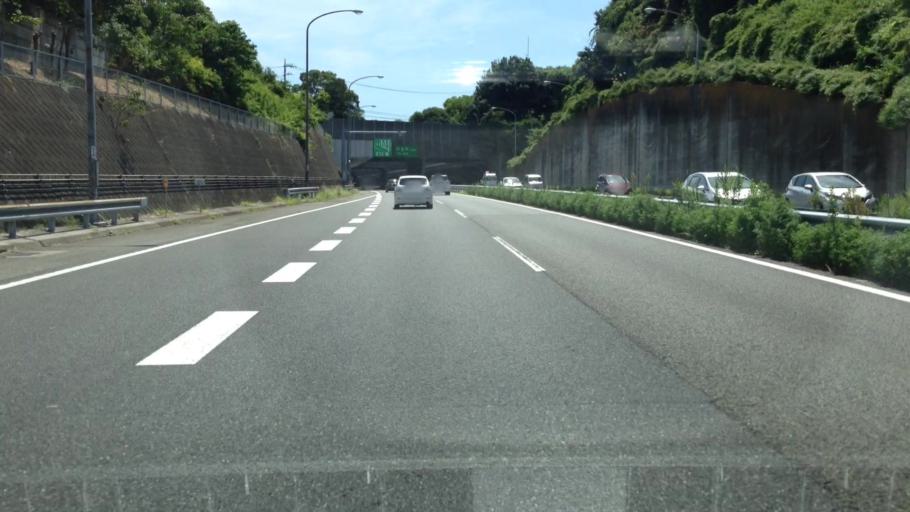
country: JP
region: Kanagawa
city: Yokohama
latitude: 35.4355
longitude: 139.5818
